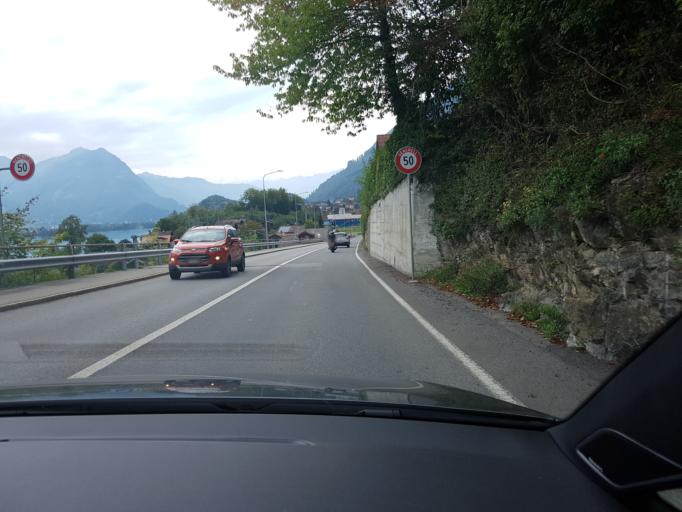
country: CH
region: Bern
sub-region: Interlaken-Oberhasli District
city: Ringgenberg
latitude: 46.7078
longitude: 7.9119
